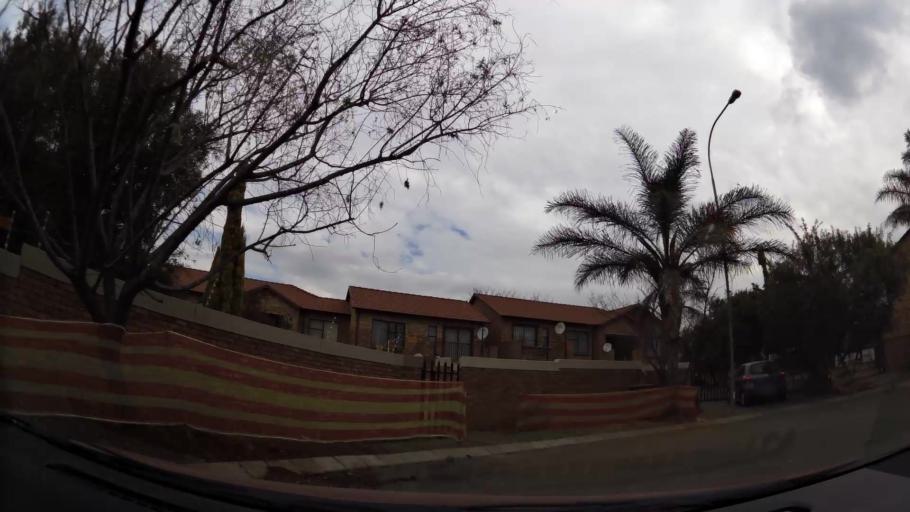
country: ZA
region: Gauteng
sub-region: West Rand District Municipality
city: Muldersdriseloop
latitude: -26.0924
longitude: 27.8716
